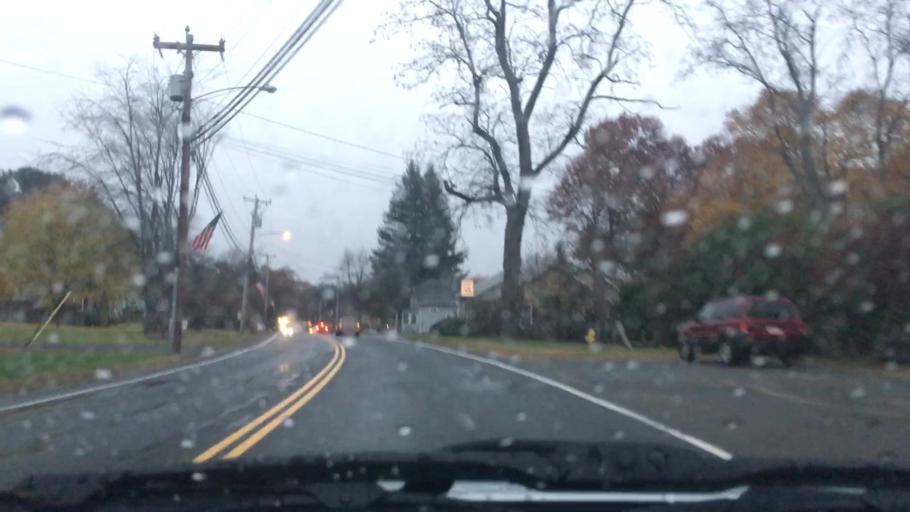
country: US
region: Massachusetts
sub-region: Hampden County
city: Southwick
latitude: 42.0622
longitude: -72.7634
